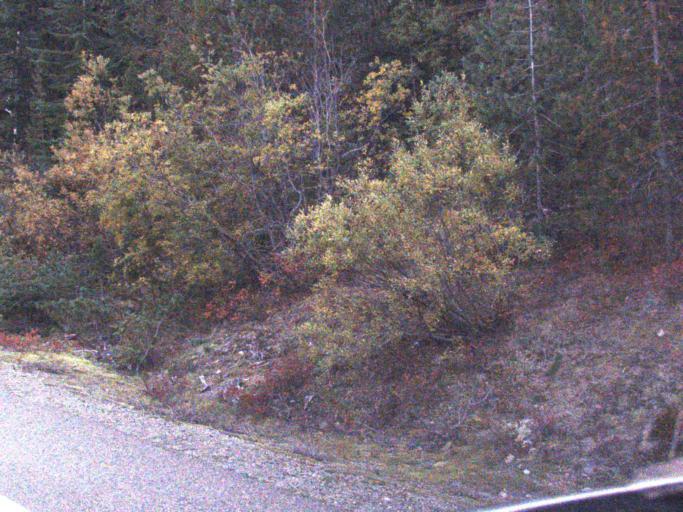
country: US
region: Washington
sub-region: Snohomish County
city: Darrington
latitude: 48.6423
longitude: -120.8534
